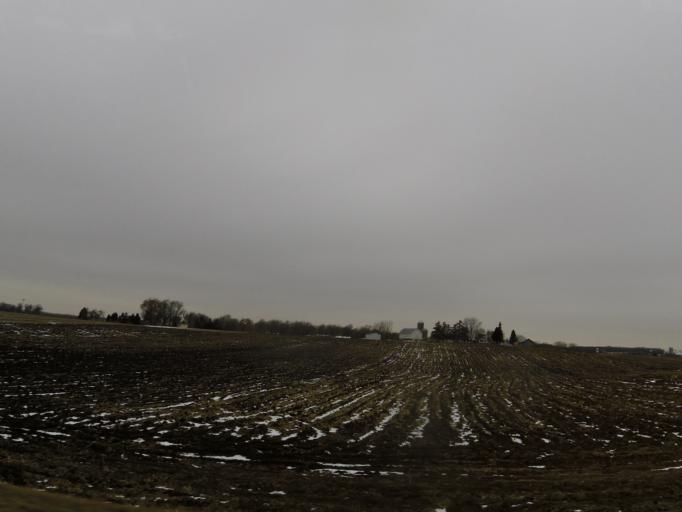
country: US
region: Minnesota
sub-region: Carver County
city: Carver
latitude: 44.7712
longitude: -93.6838
